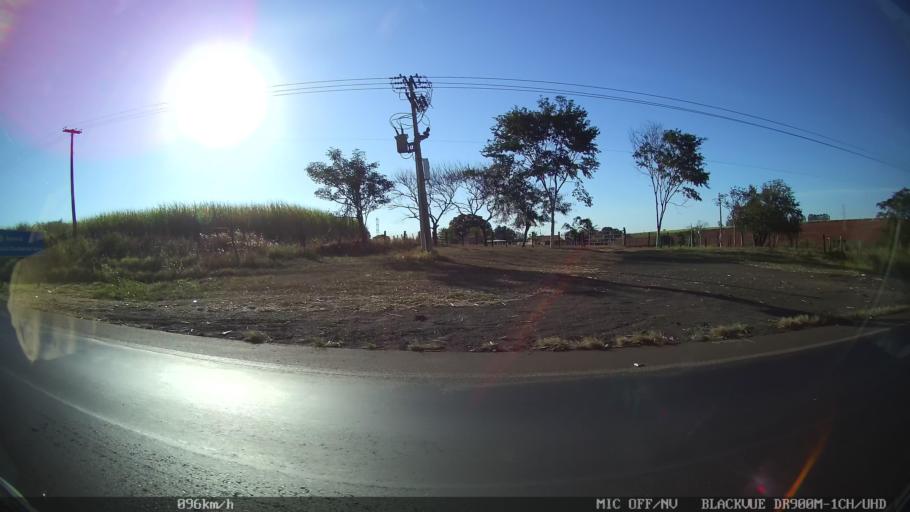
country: BR
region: Sao Paulo
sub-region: Olimpia
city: Olimpia
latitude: -20.7023
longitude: -48.9435
